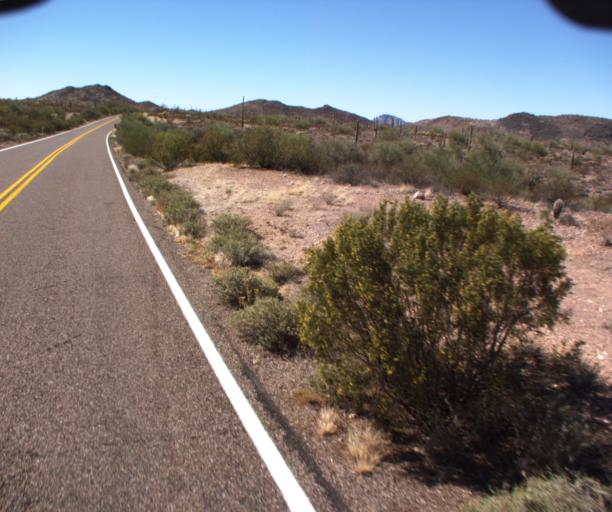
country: MX
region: Sonora
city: Sonoyta
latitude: 32.1010
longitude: -112.7712
